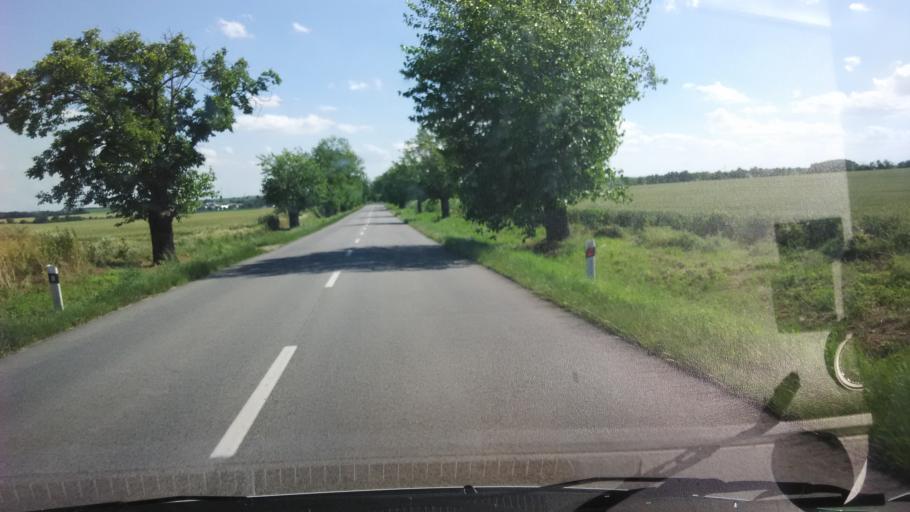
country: SK
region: Nitriansky
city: Tlmace
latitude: 48.1718
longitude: 18.4518
